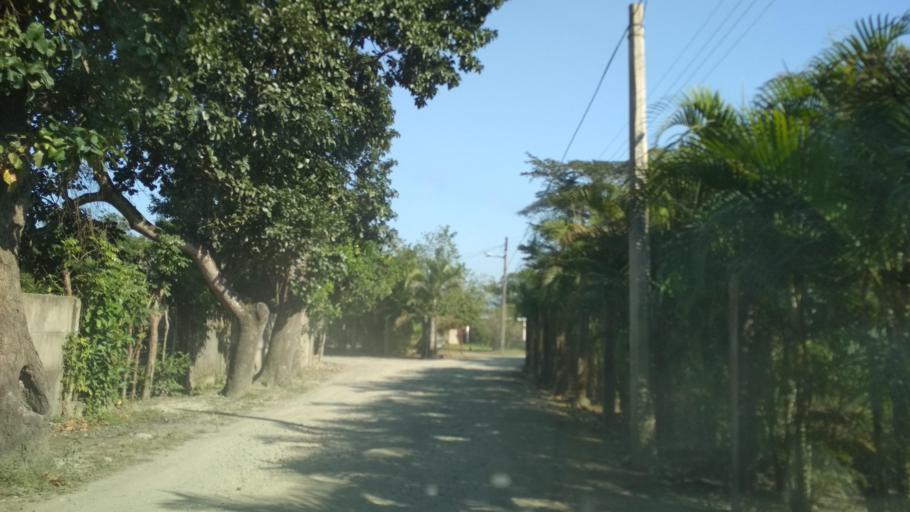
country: MX
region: Veracruz
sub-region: Martinez de la Torre
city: El Progreso
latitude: 20.0808
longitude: -97.0192
